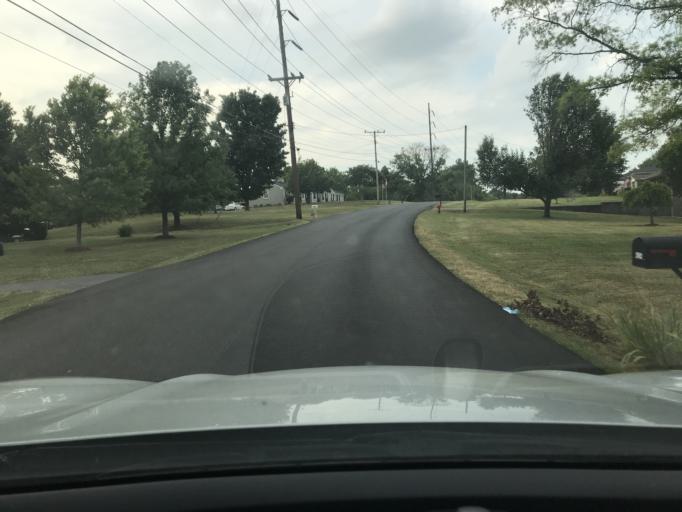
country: US
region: Tennessee
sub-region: Davidson County
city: Goodlettsville
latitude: 36.3023
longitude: -86.7150
